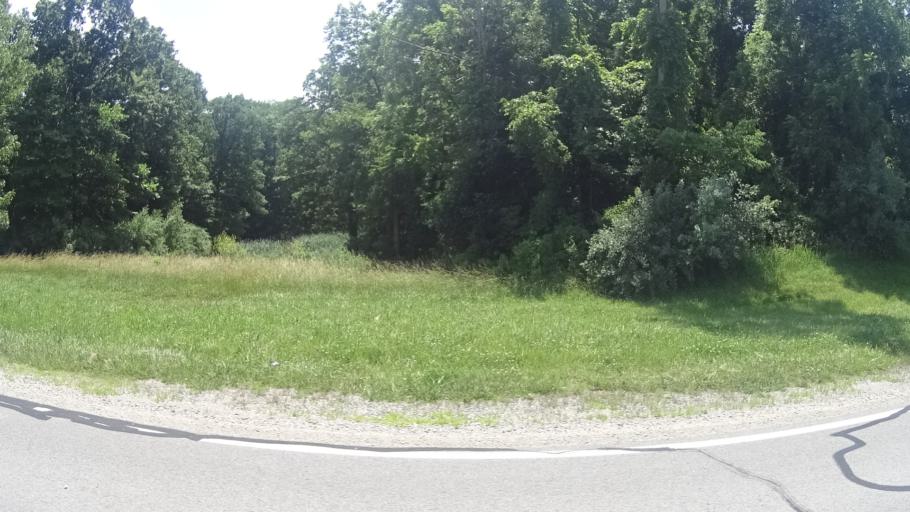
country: US
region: Ohio
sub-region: Erie County
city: Huron
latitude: 41.3689
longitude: -82.5427
